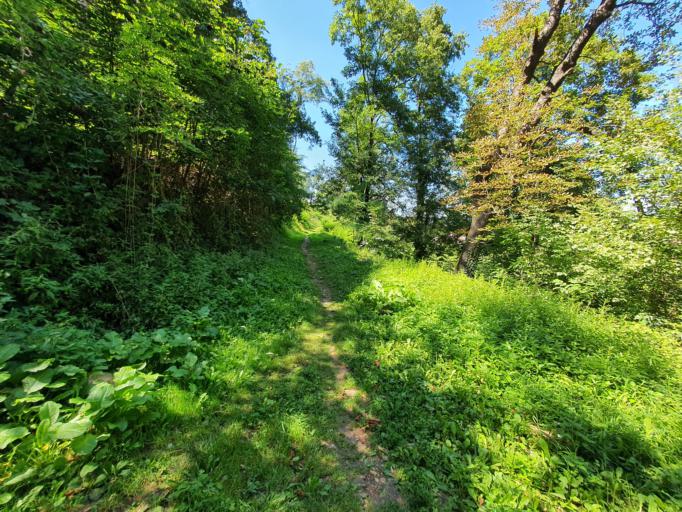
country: RS
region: Central Serbia
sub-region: Zlatiborski Okrug
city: Uzice
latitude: 43.8487
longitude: 19.8454
